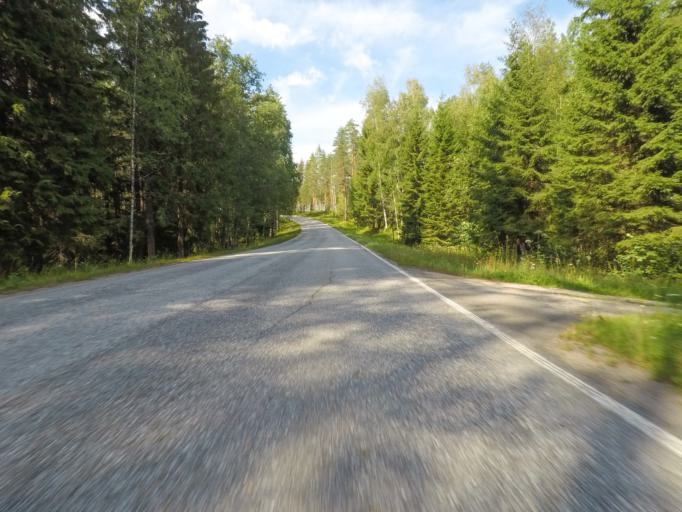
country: FI
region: Southern Savonia
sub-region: Mikkeli
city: Puumala
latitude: 61.6946
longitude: 28.2158
